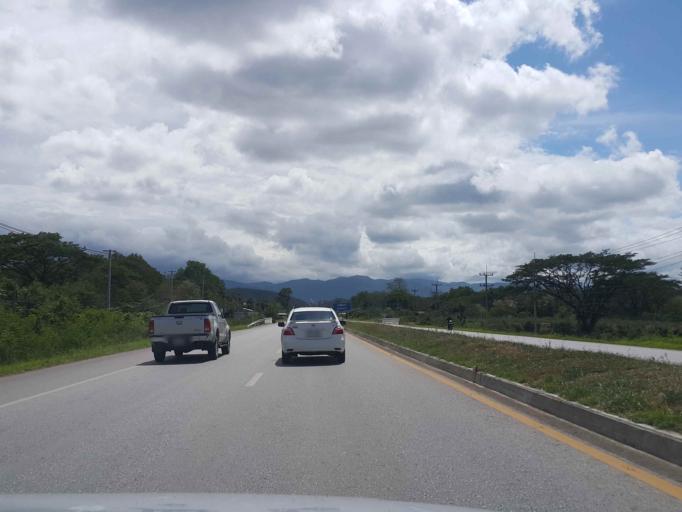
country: TH
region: Tak
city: Tak
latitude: 16.8337
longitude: 99.1000
